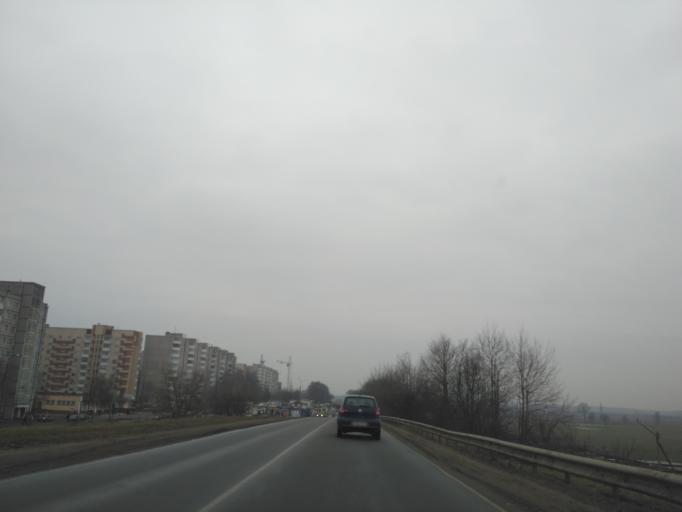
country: BY
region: Brest
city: Baranovichi
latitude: 53.1591
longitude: 26.0064
